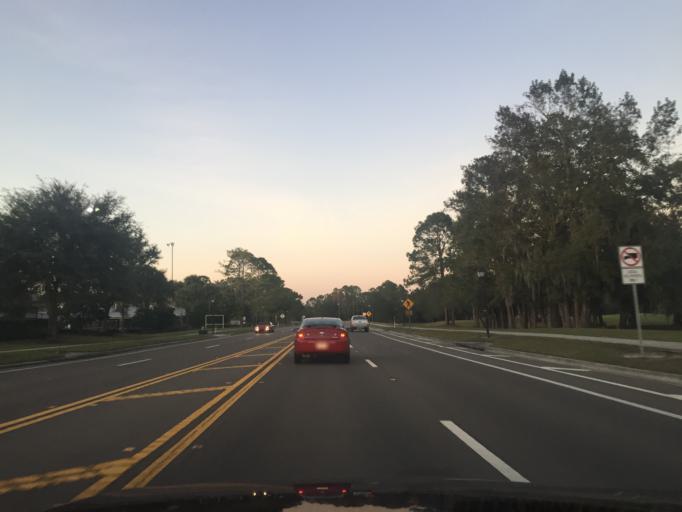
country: US
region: Florida
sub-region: Seminole County
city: Oviedo
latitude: 28.6455
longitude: -81.1767
